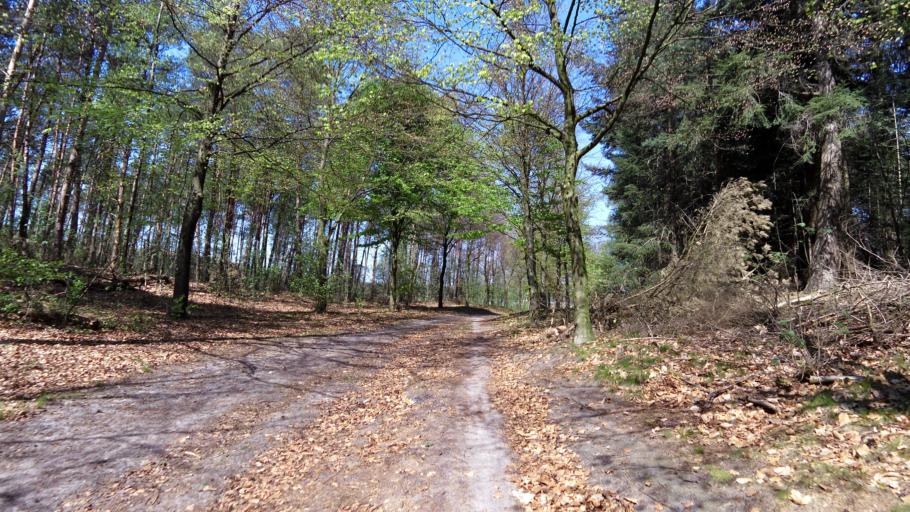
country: NL
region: Gelderland
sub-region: Gemeente Renkum
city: Oosterbeek
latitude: 52.0238
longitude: 5.8392
